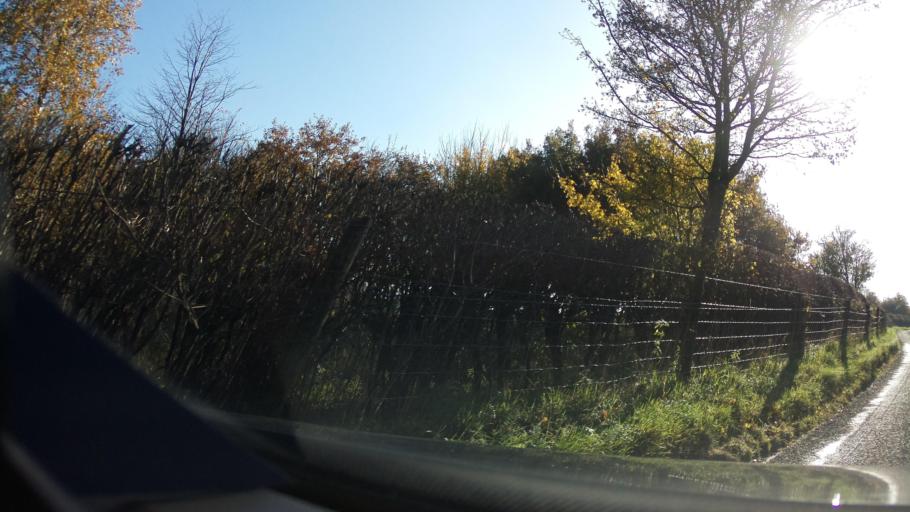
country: GB
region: England
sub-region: Somerset
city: Bruton
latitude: 51.1459
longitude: -2.4245
